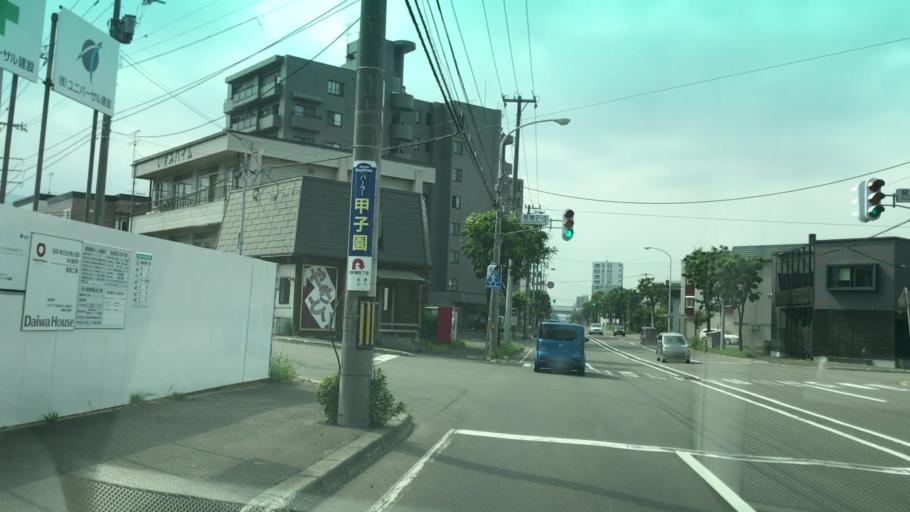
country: JP
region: Hokkaido
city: Sapporo
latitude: 43.0899
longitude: 141.2896
